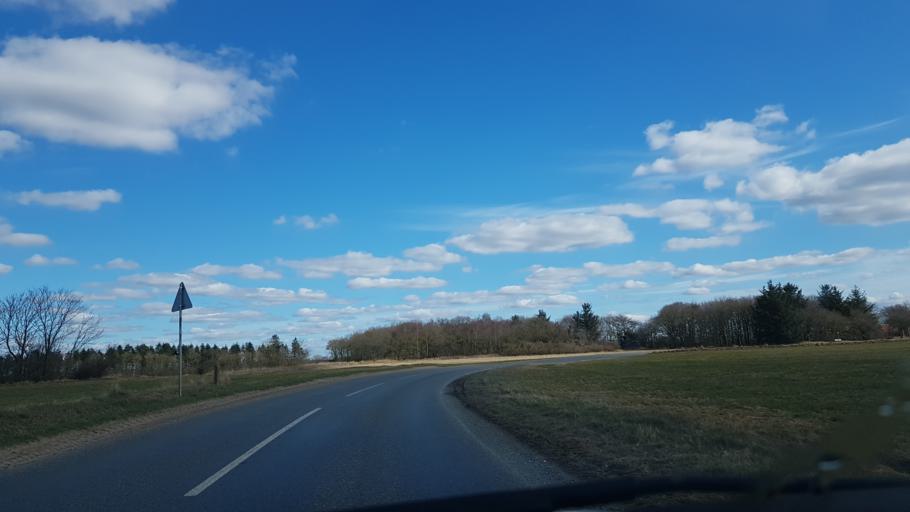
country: DK
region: South Denmark
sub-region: Esbjerg Kommune
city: Ribe
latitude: 55.4049
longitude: 8.8076
